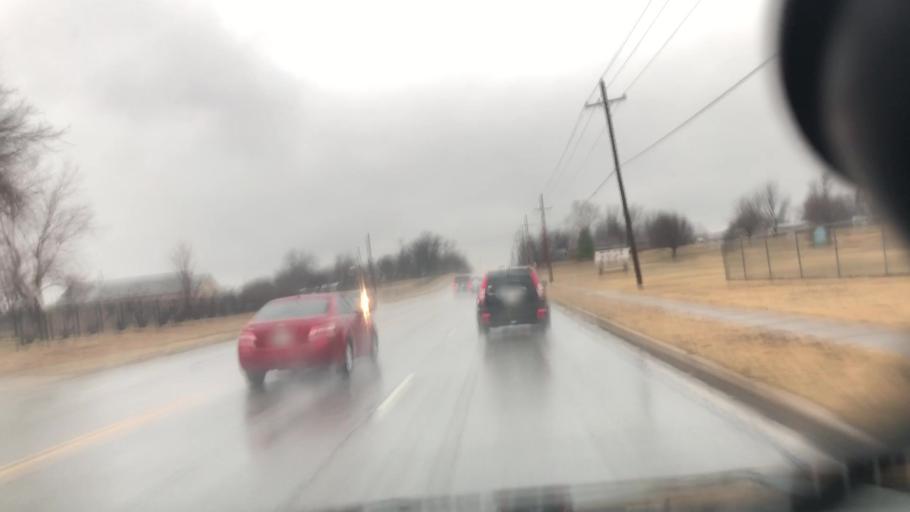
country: US
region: Oklahoma
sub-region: Rogers County
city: Catoosa
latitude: 36.1458
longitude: -95.8333
